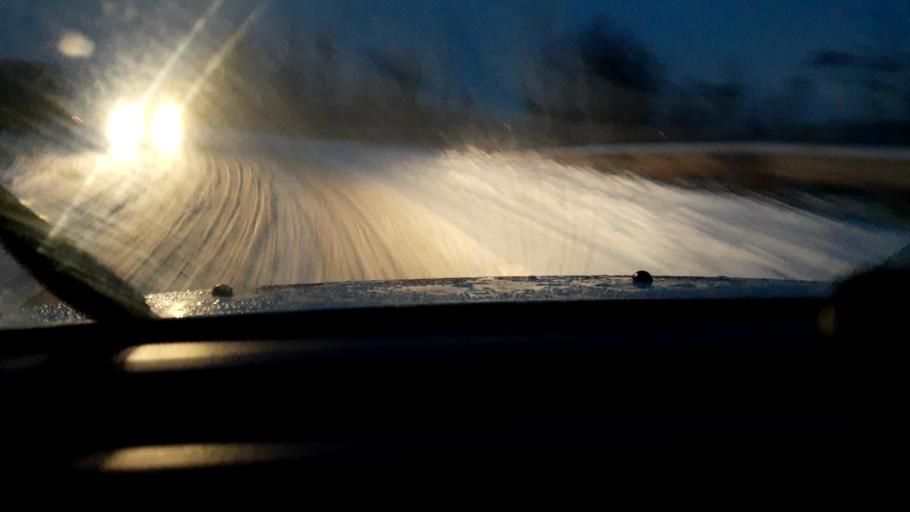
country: RU
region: Nizjnij Novgorod
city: Burevestnik
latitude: 56.1996
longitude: 43.8908
